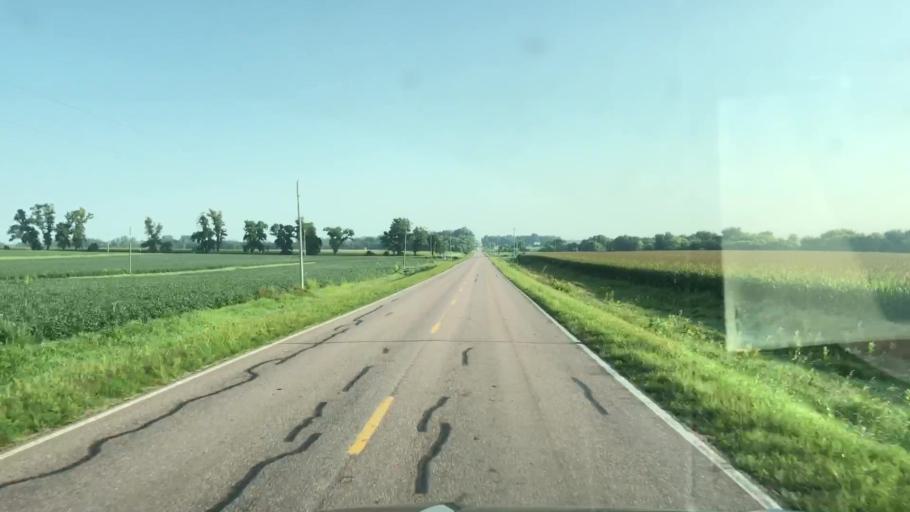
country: US
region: Iowa
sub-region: Lyon County
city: George
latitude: 43.2409
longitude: -96.0005
